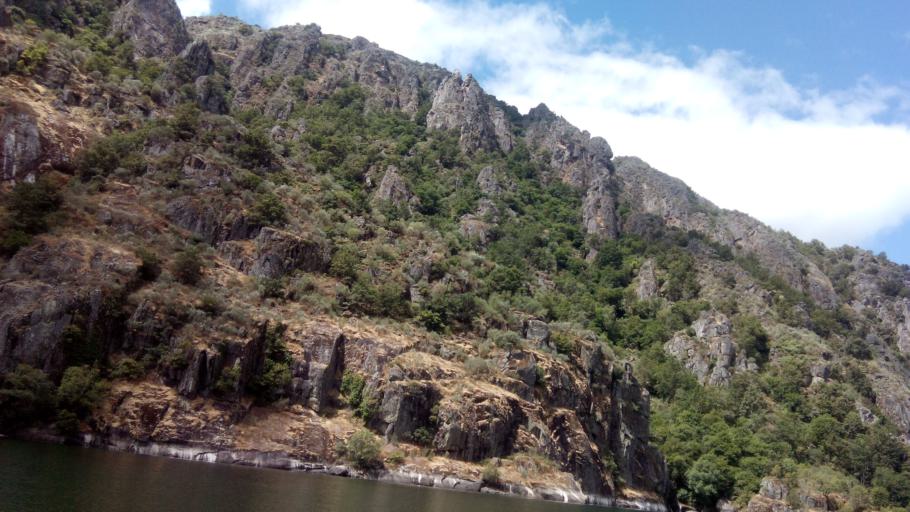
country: ES
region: Galicia
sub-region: Provincia de Lugo
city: Sober
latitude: 42.3863
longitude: -7.6197
